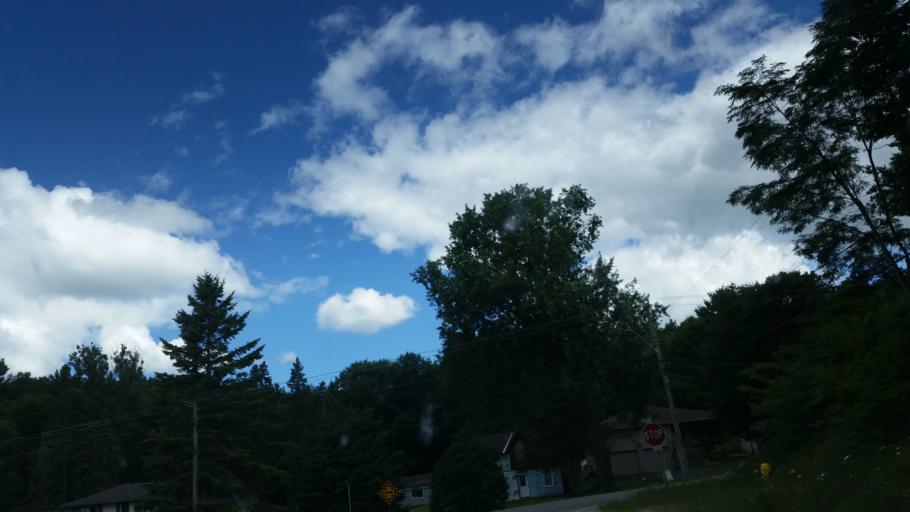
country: CA
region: Ontario
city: Barrie
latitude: 44.4503
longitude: -79.7308
